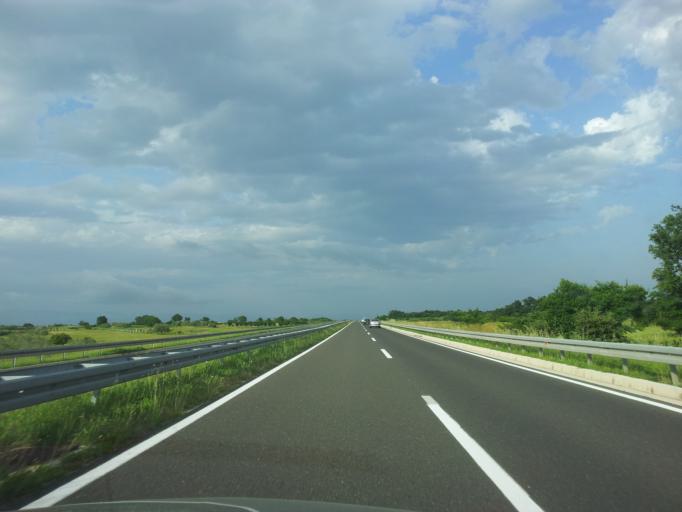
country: HR
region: Zadarska
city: Galovac
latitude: 44.0958
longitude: 15.3749
